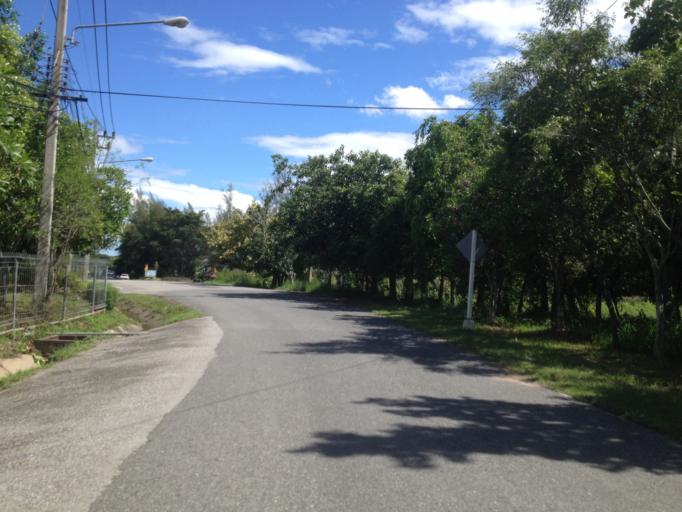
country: TH
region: Chiang Mai
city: Hang Dong
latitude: 18.7480
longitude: 98.9197
